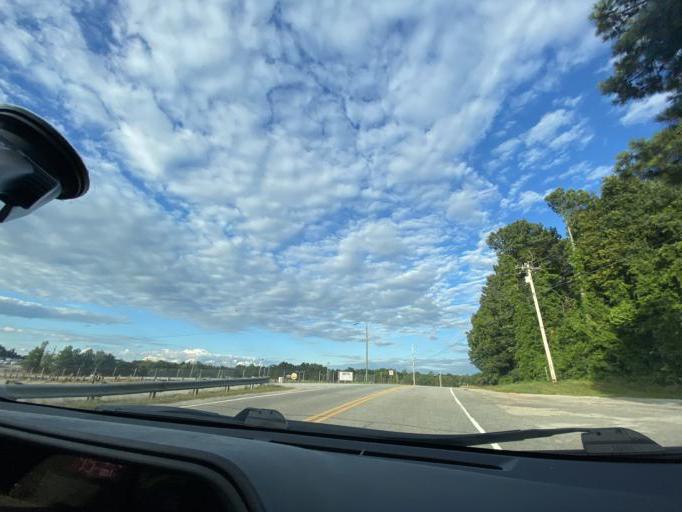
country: US
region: Georgia
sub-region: Fulton County
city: Palmetto
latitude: 33.4469
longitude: -84.6846
